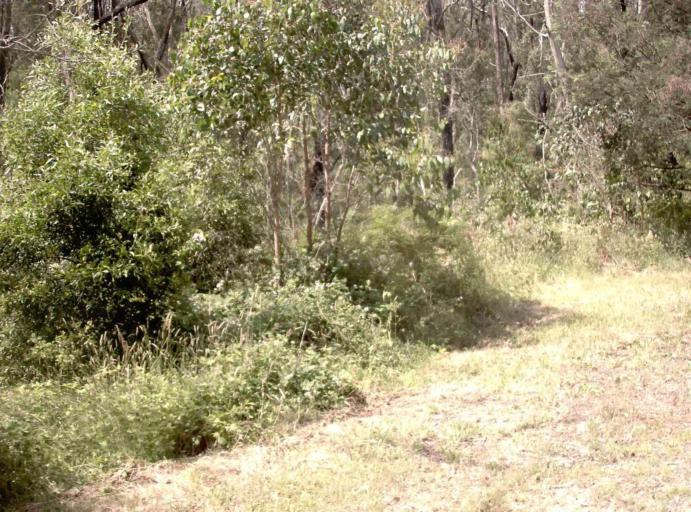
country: AU
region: Victoria
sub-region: Latrobe
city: Traralgon
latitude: -38.3065
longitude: 146.5491
